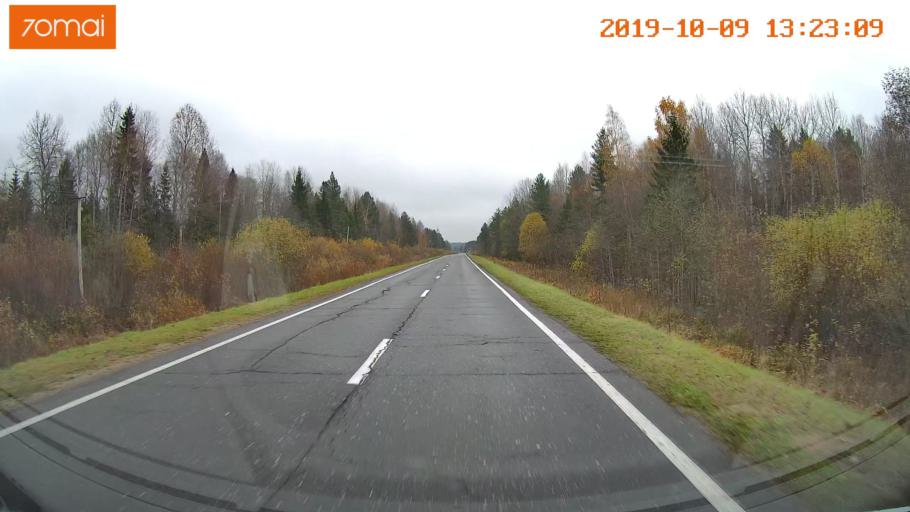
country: RU
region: Jaroslavl
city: Lyubim
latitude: 58.3365
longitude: 40.8820
